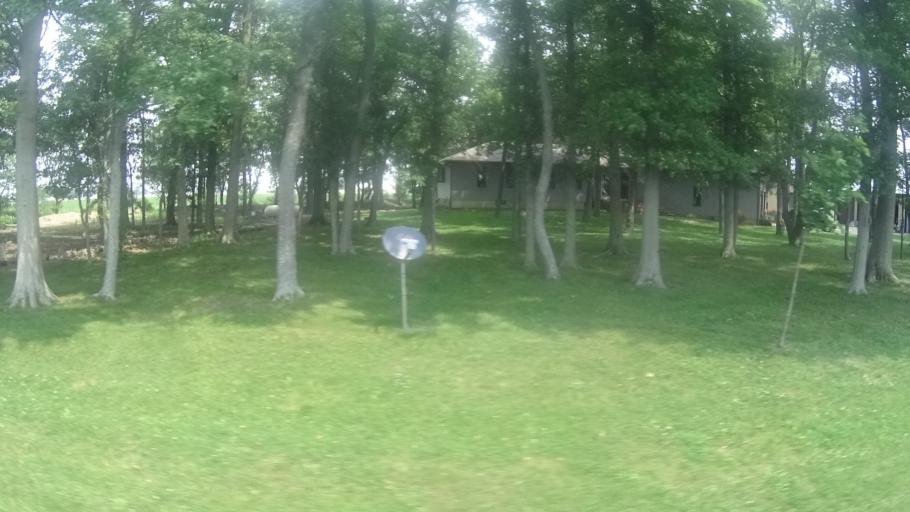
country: US
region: Ohio
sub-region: Huron County
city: Monroeville
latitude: 41.3338
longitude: -82.7153
